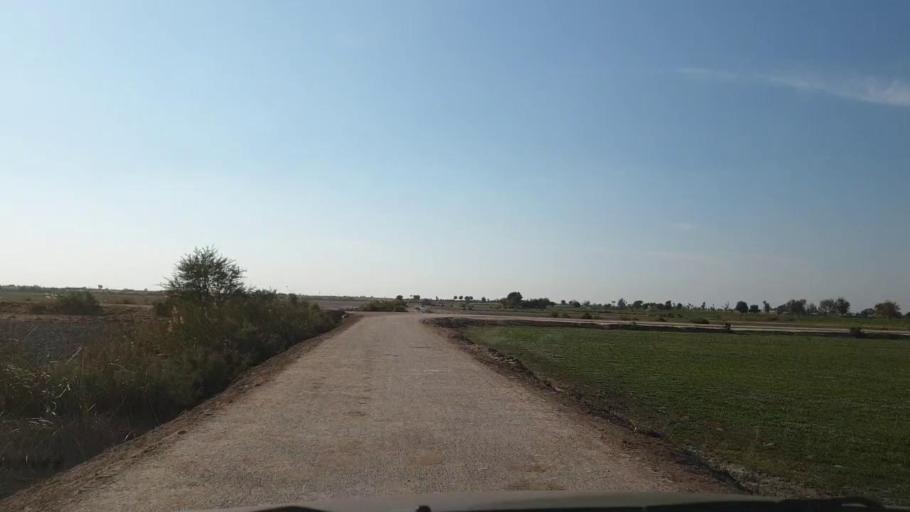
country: PK
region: Sindh
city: Khadro
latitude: 26.1550
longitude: 68.7544
